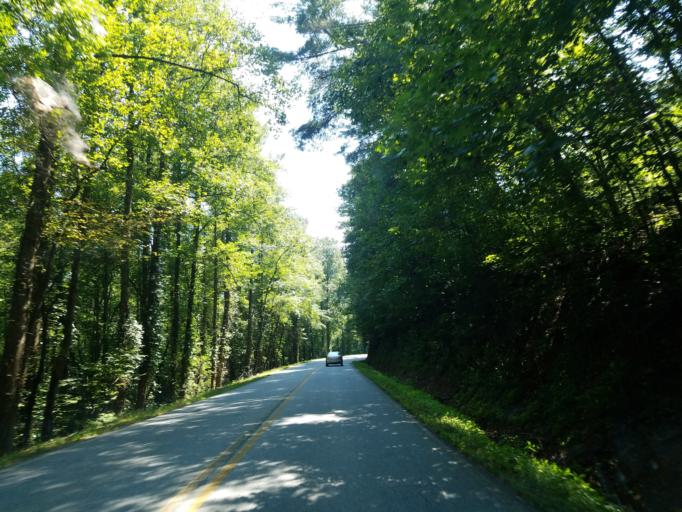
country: US
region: Georgia
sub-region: Lumpkin County
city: Dahlonega
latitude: 34.6301
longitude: -83.9357
